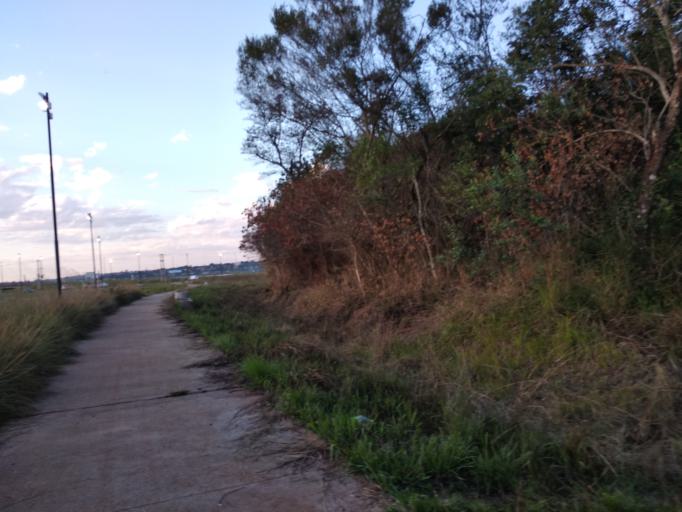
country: AR
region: Misiones
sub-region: Departamento de Capital
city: Posadas
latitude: -27.3974
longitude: -55.9557
